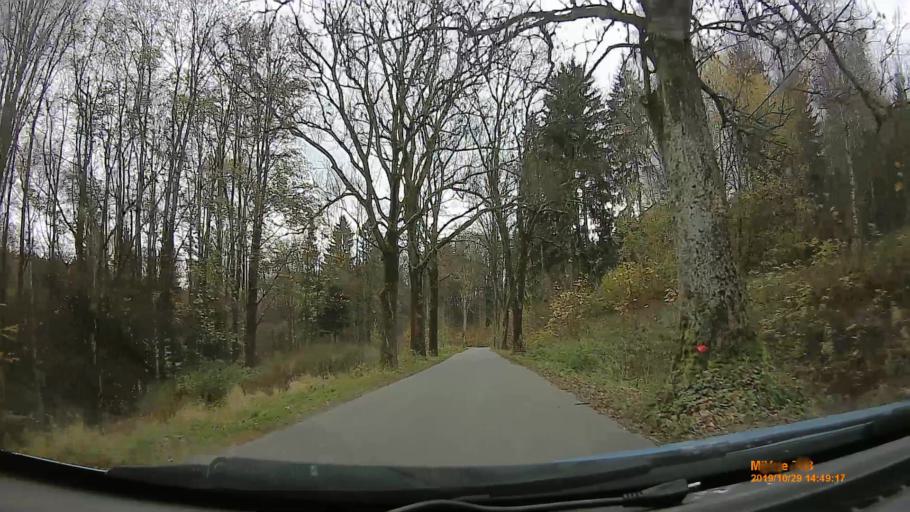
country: PL
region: Lower Silesian Voivodeship
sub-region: Powiat klodzki
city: Szczytna
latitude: 50.4340
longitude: 16.4338
